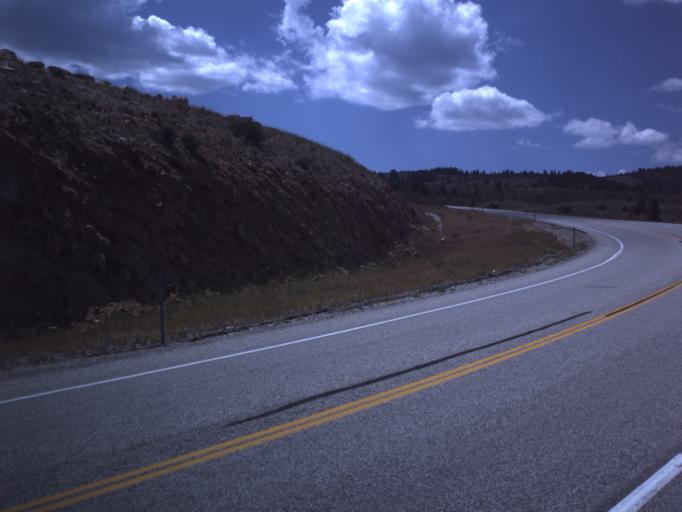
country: US
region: Idaho
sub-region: Bear Lake County
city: Paris
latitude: 41.9319
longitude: -111.4349
